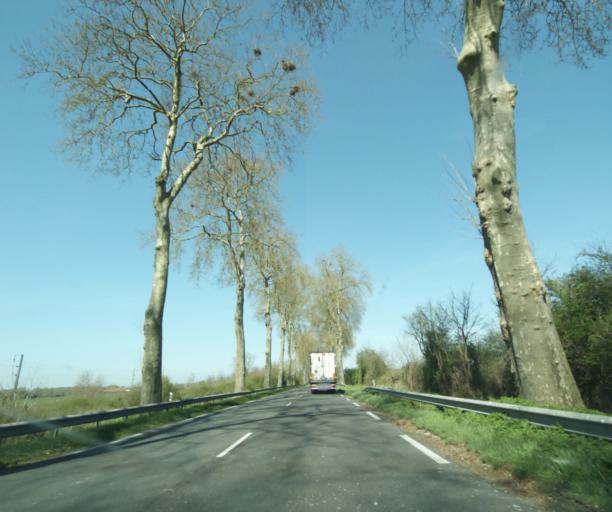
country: FR
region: Bourgogne
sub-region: Departement de la Nievre
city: Chantenay-Saint-Imbert
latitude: 46.7200
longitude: 3.1829
